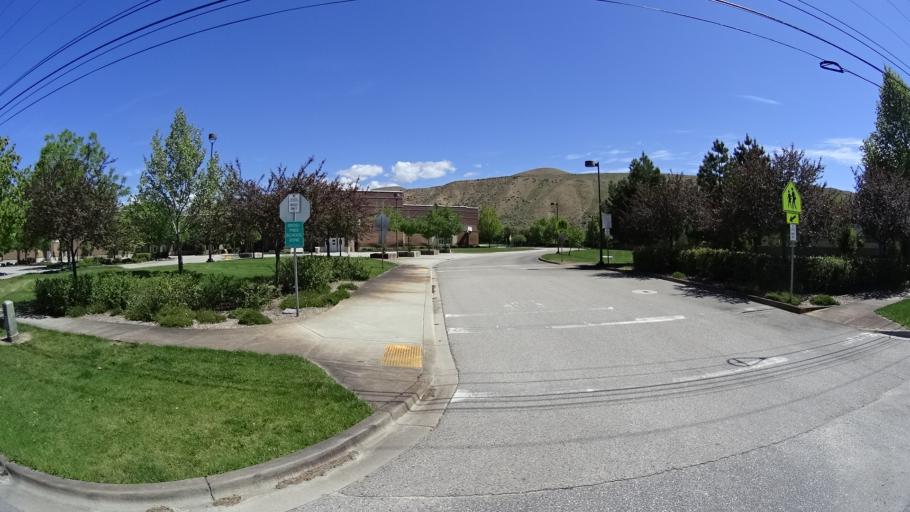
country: US
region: Idaho
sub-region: Ada County
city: Boise
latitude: 43.5649
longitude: -116.1134
